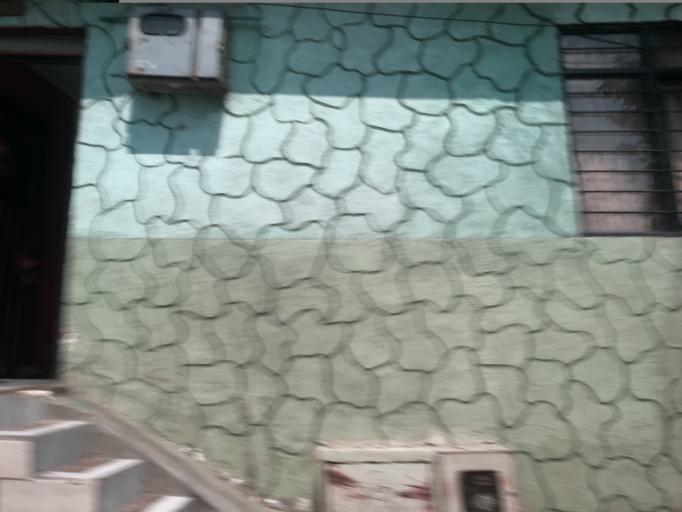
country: CO
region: Valle del Cauca
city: Cali
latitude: 3.4521
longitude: -76.5734
